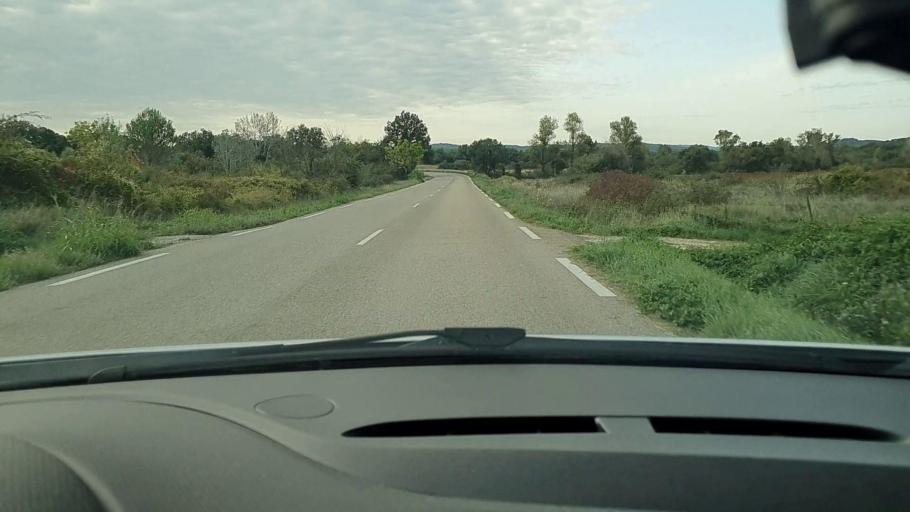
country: FR
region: Languedoc-Roussillon
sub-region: Departement du Gard
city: Mons
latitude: 44.0843
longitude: 4.2182
